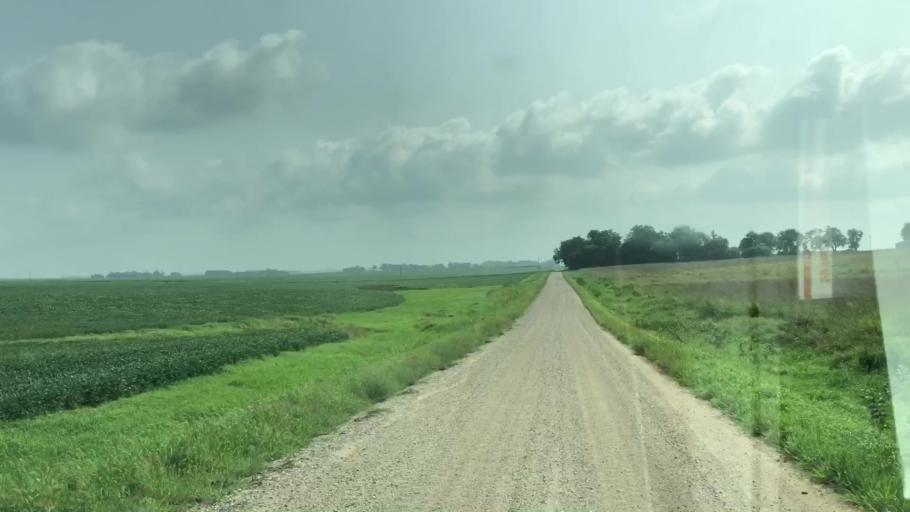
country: US
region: Iowa
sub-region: O'Brien County
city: Sheldon
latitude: 43.2005
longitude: -95.8883
